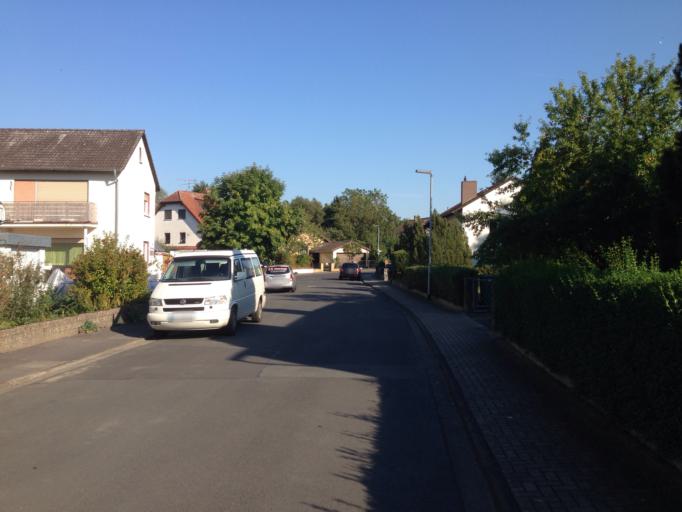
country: DE
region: Hesse
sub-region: Regierungsbezirk Giessen
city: Giessen
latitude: 50.5416
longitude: 8.7249
